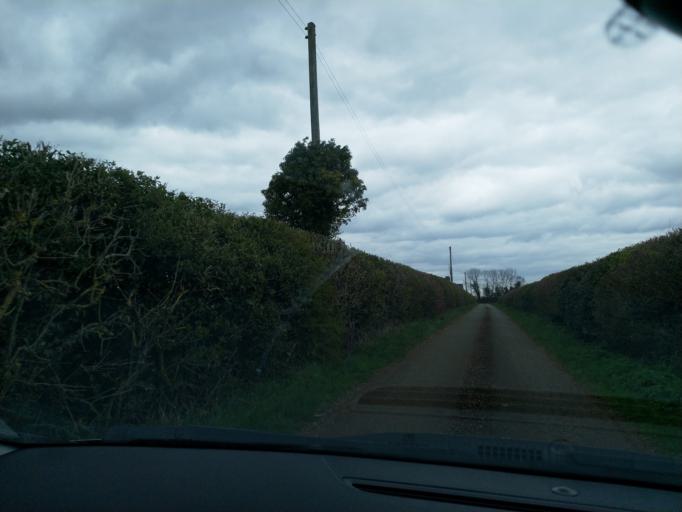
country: GB
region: England
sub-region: Oxfordshire
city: Hanwell
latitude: 52.1155
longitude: -1.4676
